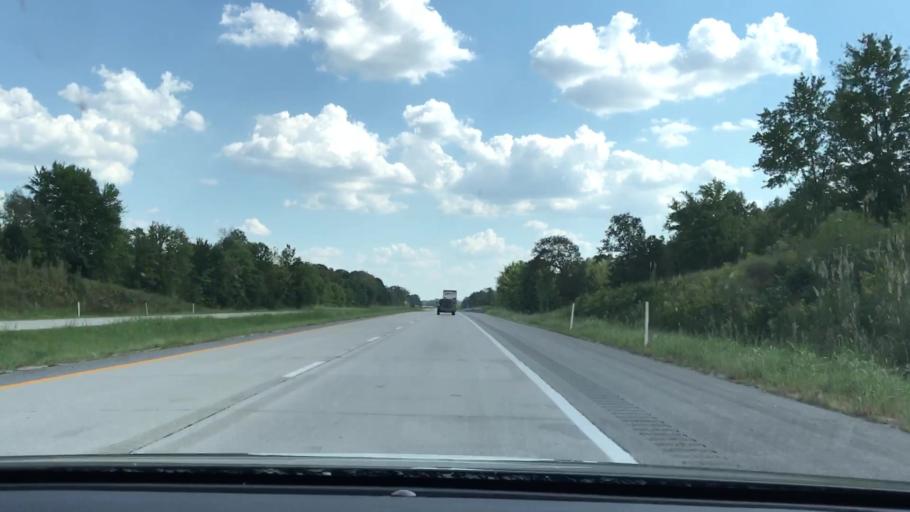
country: US
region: Kentucky
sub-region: Ohio County
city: Oak Grove
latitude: 37.3654
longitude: -86.7973
